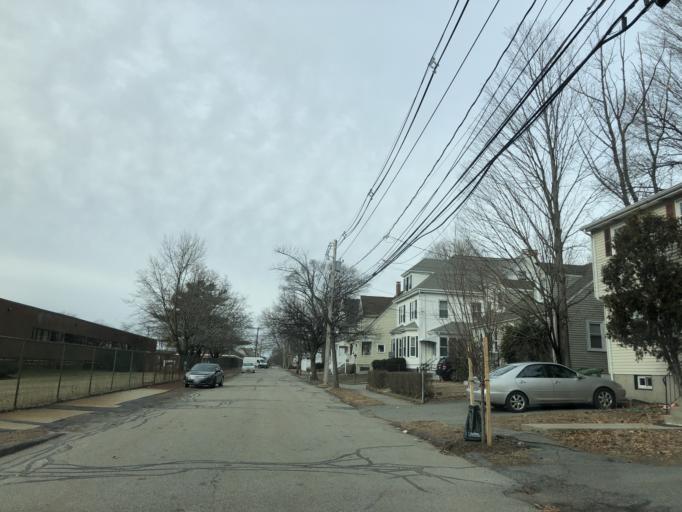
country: US
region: Massachusetts
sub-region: Middlesex County
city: Watertown
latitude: 42.3656
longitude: -71.1627
